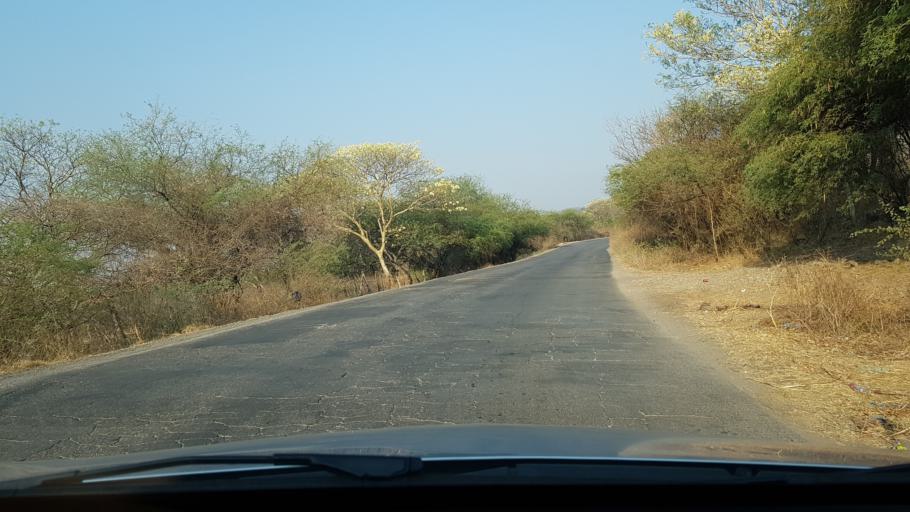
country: MX
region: Morelos
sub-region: Tepalcingo
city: Zacapalco
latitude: 18.6370
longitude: -99.0112
